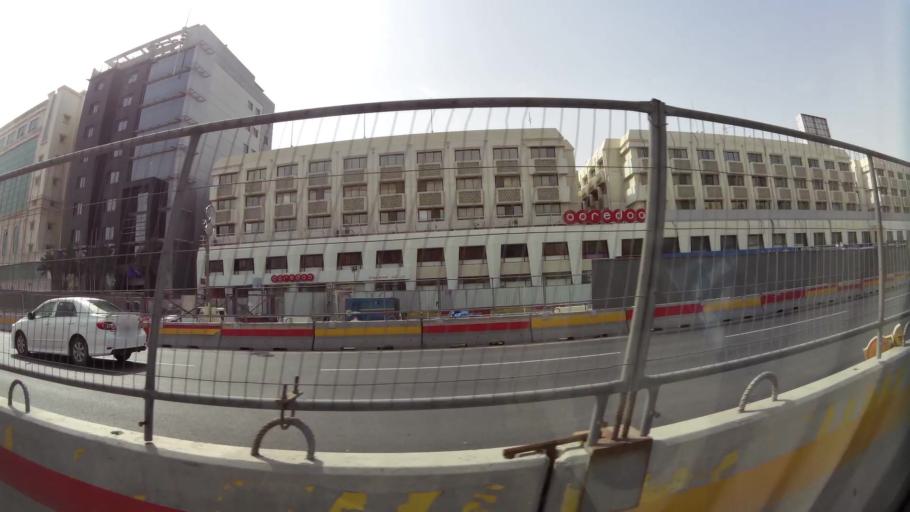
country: QA
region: Baladiyat ad Dawhah
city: Doha
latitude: 25.2807
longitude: 51.4965
